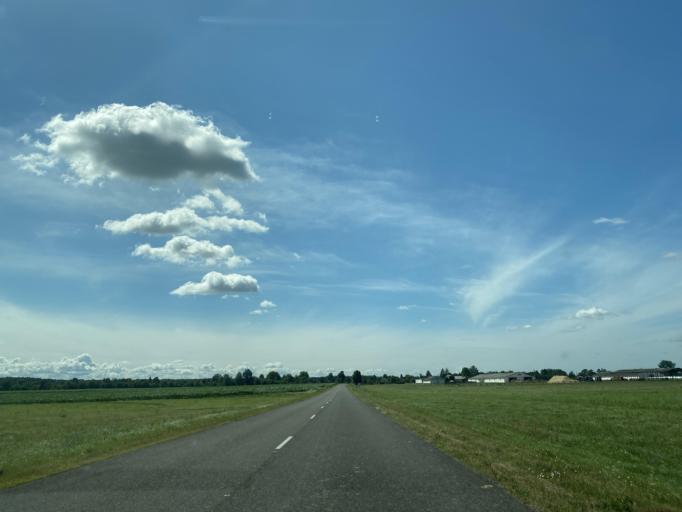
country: BY
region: Brest
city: Ivanava
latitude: 52.2139
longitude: 25.6296
